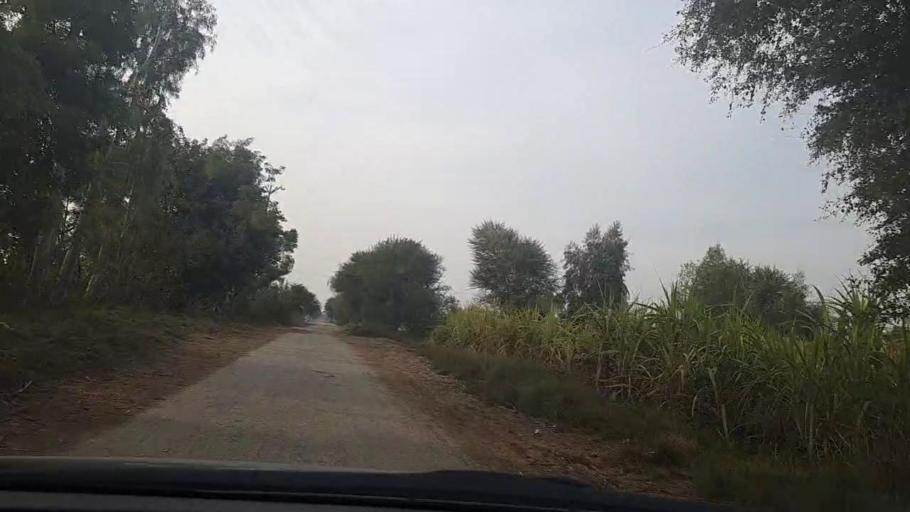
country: PK
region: Sindh
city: Daulatpur
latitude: 26.3353
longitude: 68.0387
